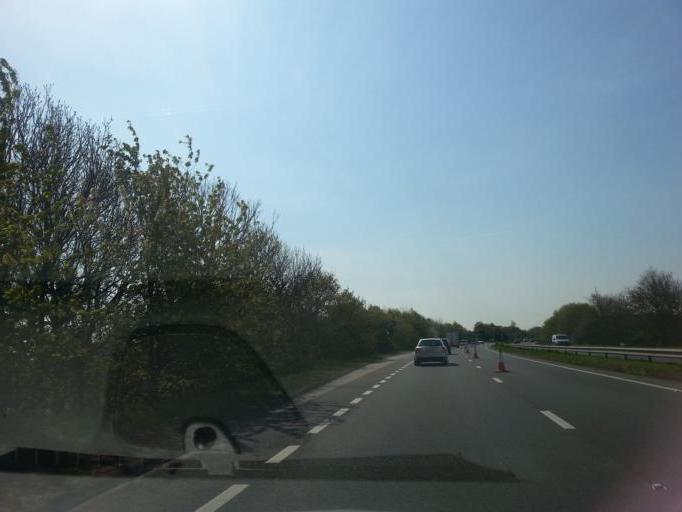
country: GB
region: England
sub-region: Suffolk
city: Kesgrave
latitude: 52.0316
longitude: 1.2579
